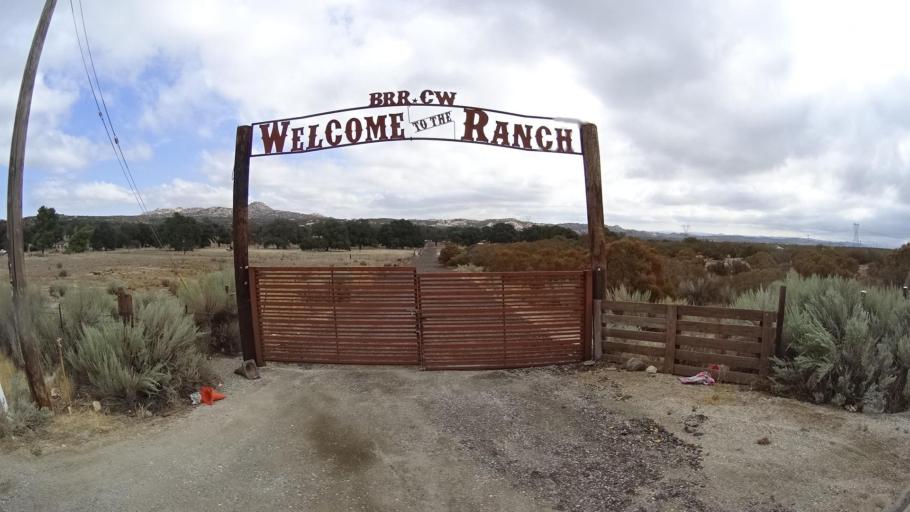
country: MX
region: Baja California
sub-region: Tecate
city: Cereso del Hongo
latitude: 32.6116
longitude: -116.3203
